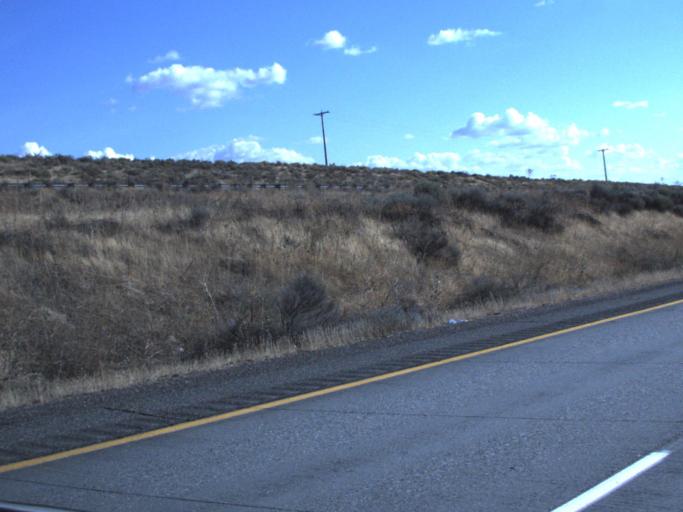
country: US
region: Washington
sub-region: Benton County
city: Highland
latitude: 46.0584
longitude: -119.2241
